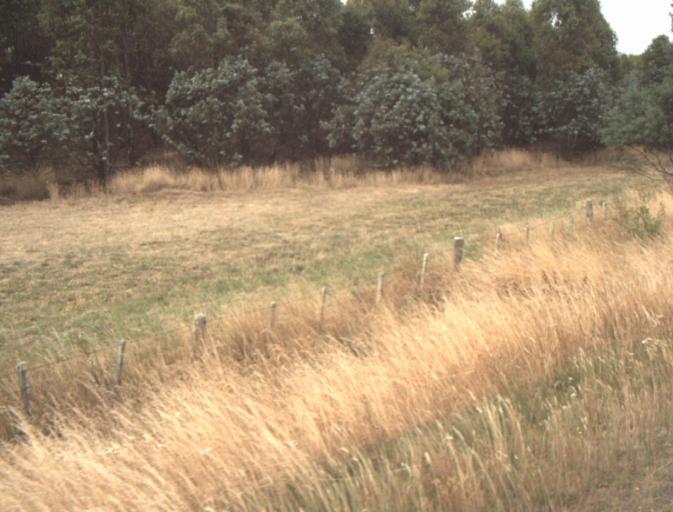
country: AU
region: Tasmania
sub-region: Northern Midlands
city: Evandale
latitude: -41.4758
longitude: 147.5189
